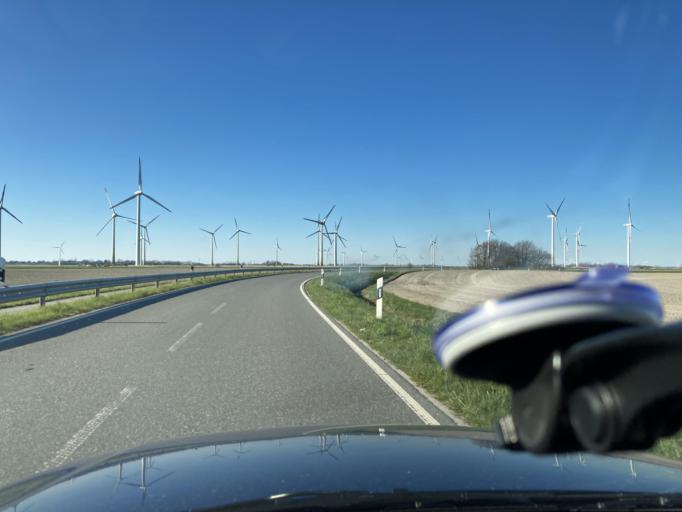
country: DE
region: Schleswig-Holstein
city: Schulp
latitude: 54.2261
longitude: 8.9498
